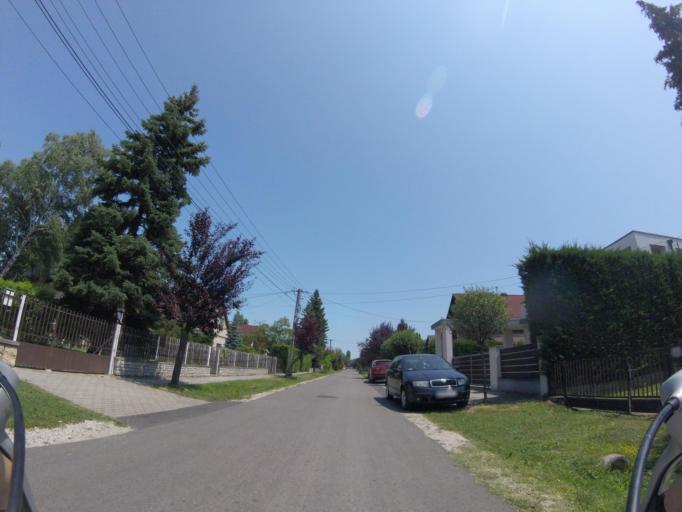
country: HU
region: Somogy
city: Balatonboglar
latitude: 46.7746
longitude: 17.6382
